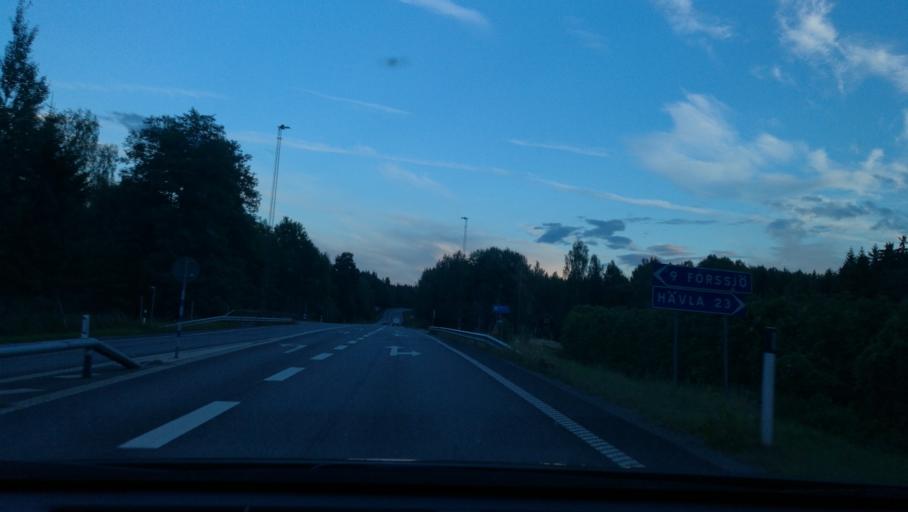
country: SE
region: Soedermanland
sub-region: Katrineholms Kommun
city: Katrineholm
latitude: 58.9057
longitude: 16.2010
